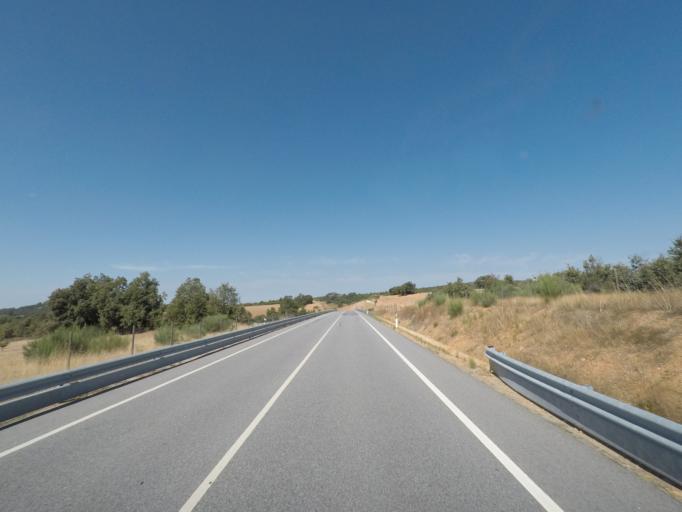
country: PT
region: Braganca
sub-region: Mogadouro
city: Mogadouro
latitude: 41.3463
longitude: -6.6341
